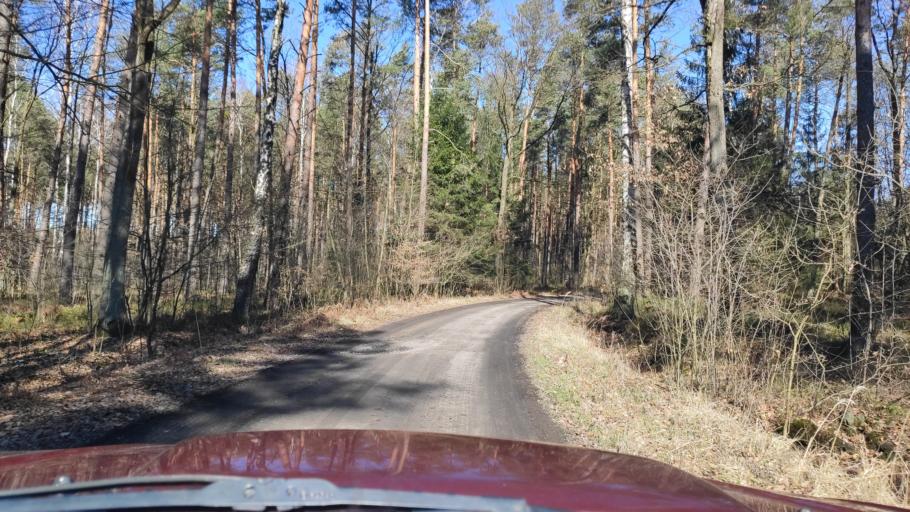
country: PL
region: Masovian Voivodeship
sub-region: Powiat kozienicki
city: Garbatka-Letnisko
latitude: 51.4455
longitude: 21.5350
